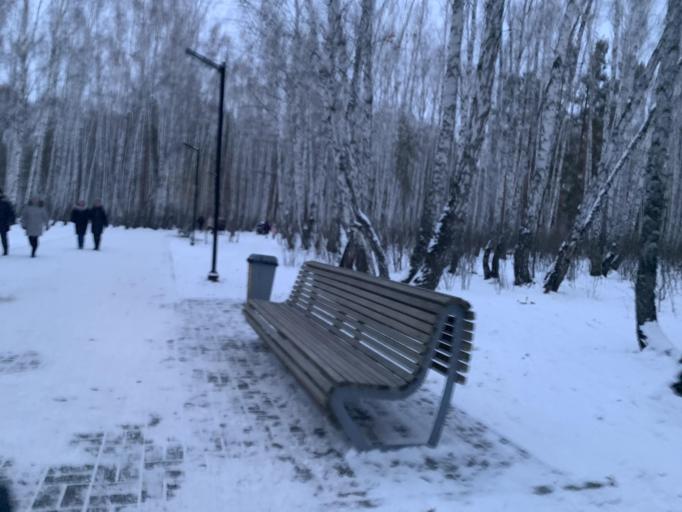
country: RU
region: Chelyabinsk
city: Roshchino
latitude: 55.1960
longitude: 61.2909
